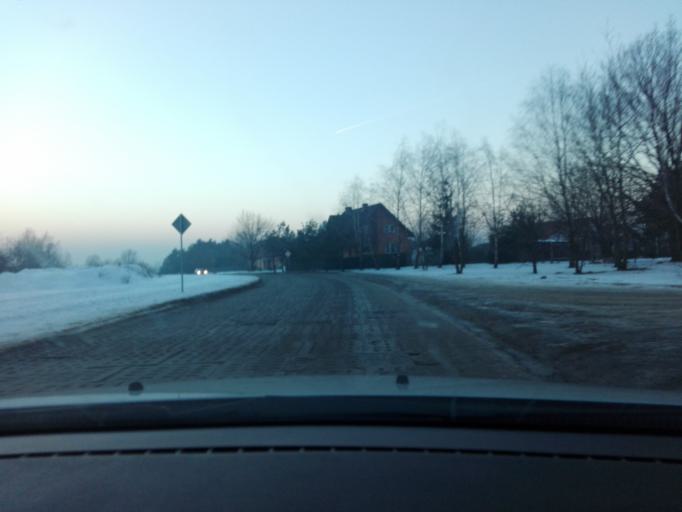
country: PL
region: Lodz Voivodeship
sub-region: Powiat zgierski
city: Zgierz
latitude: 51.8732
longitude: 19.4048
